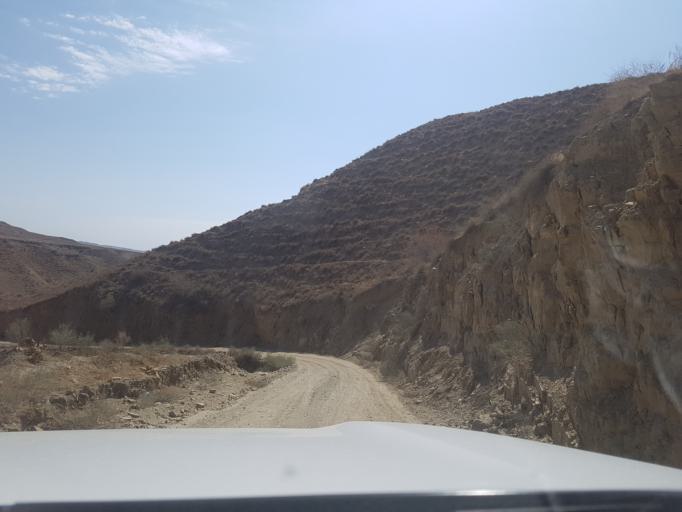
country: TM
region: Ahal
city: Baharly
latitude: 38.2401
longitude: 56.8897
